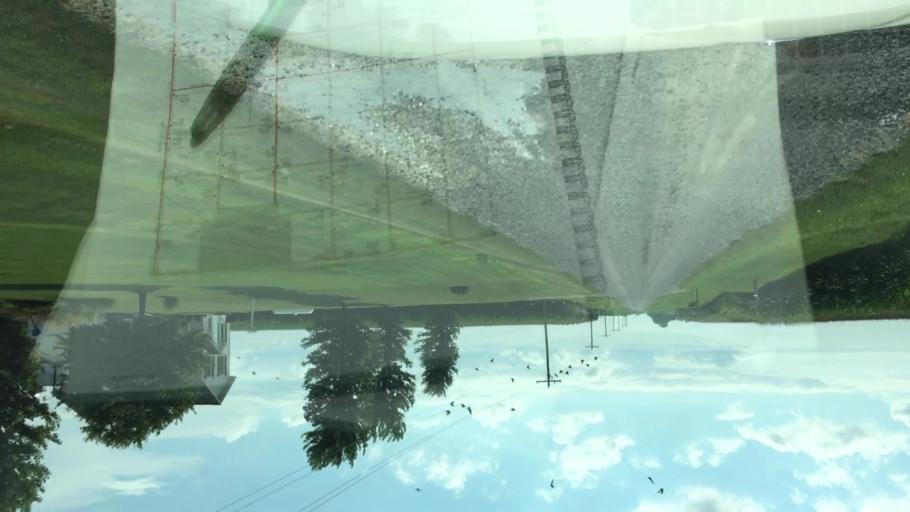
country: US
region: Illinois
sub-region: Hancock County
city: Nauvoo
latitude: 40.5213
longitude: -91.2765
